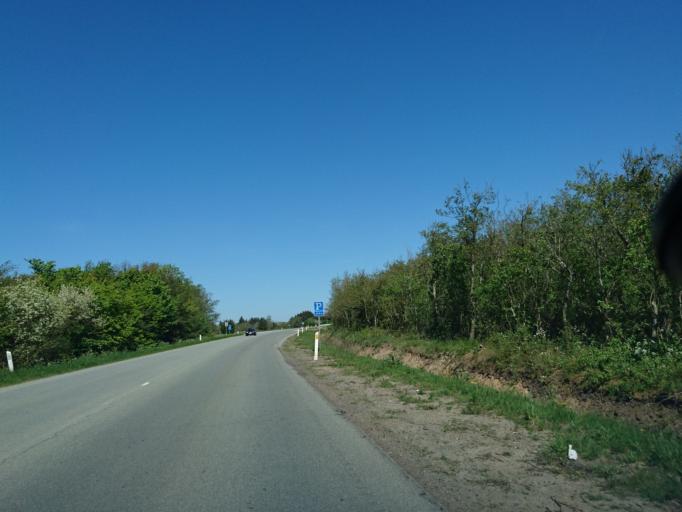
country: DK
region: North Denmark
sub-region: Hjorring Kommune
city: Hjorring
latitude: 57.4872
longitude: 10.0017
